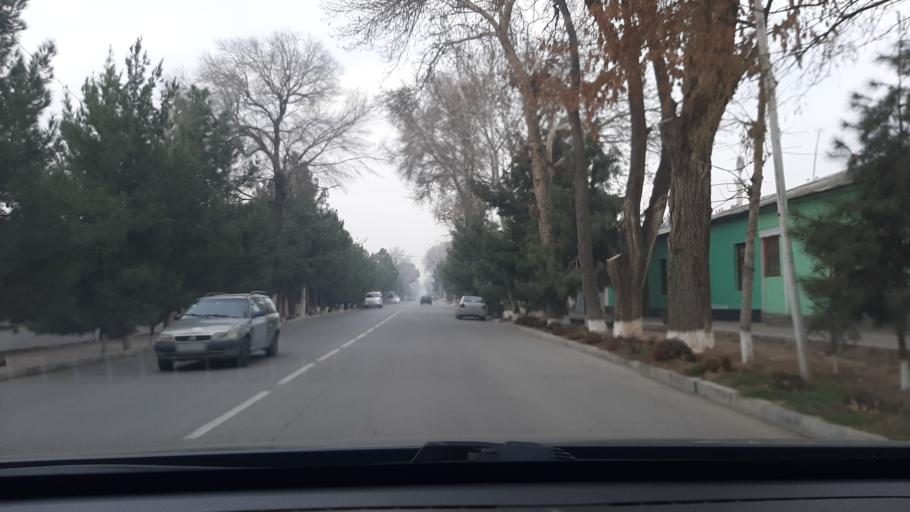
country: TJ
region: Viloyati Sughd
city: Palos
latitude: 40.2677
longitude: 69.8035
